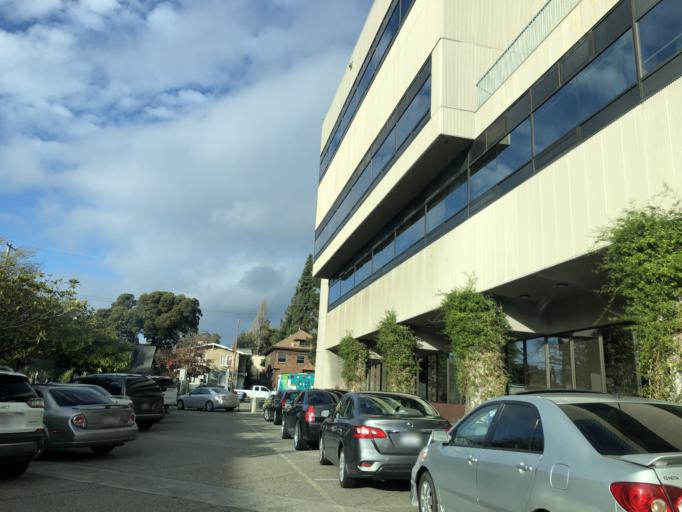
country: US
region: California
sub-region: Alameda County
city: Berkeley
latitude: 37.8558
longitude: -122.2578
